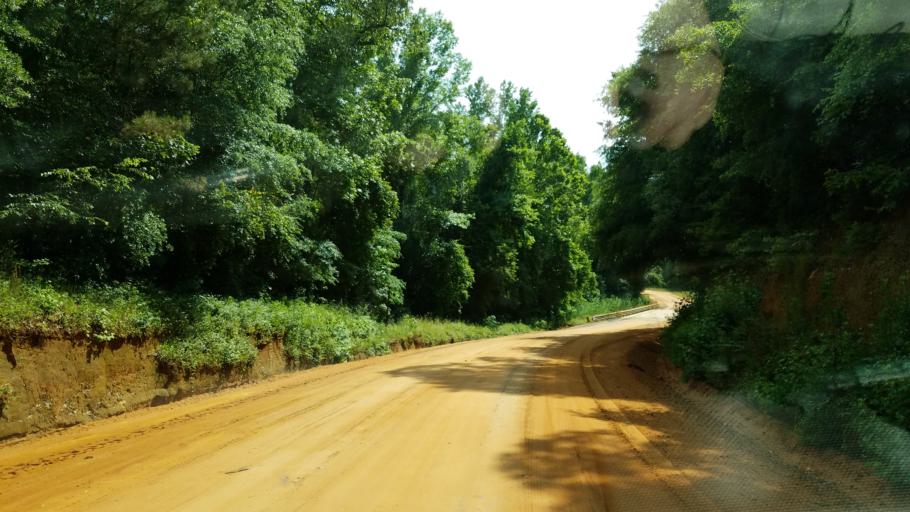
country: US
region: Georgia
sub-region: Houston County
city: Perry
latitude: 32.4560
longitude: -83.7780
